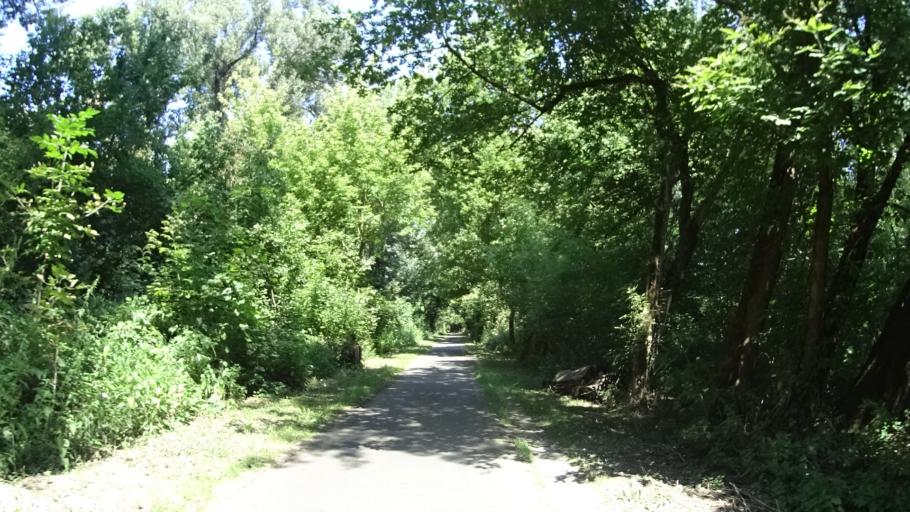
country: HU
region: Pest
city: Szodliget
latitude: 47.7523
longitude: 19.1368
